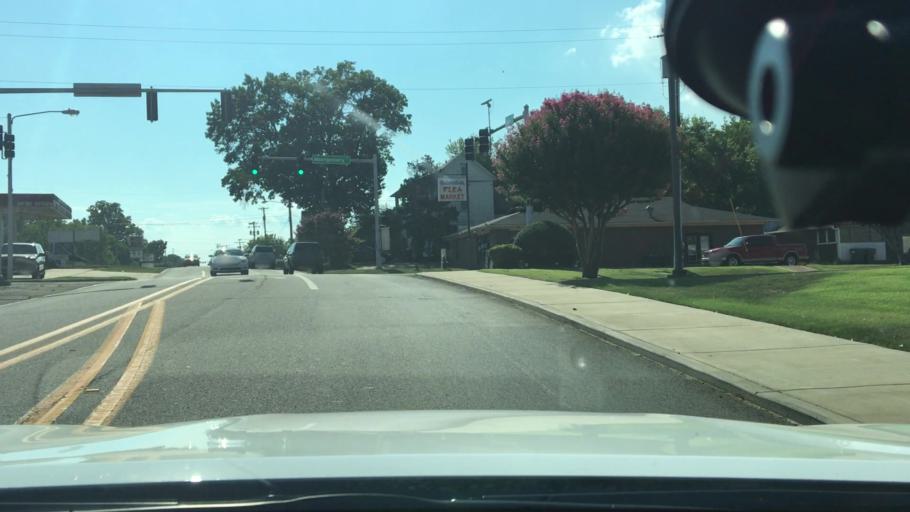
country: US
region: Arkansas
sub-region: Johnson County
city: Clarksville
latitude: 35.4714
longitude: -93.4736
